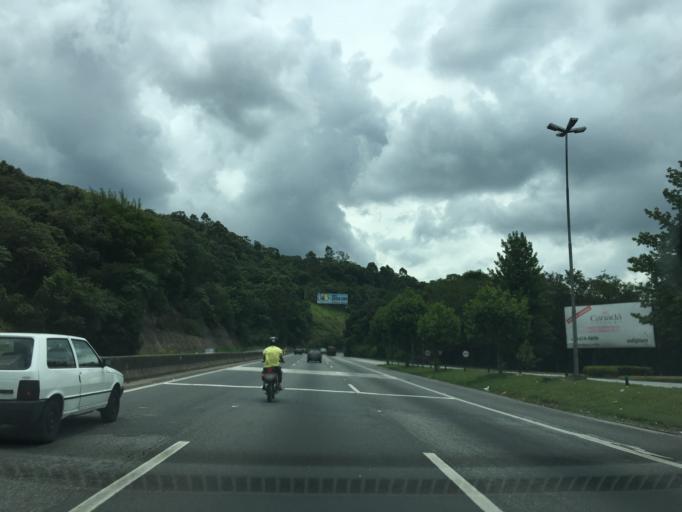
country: BR
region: Sao Paulo
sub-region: Mairipora
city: Mairipora
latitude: -23.2920
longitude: -46.5764
